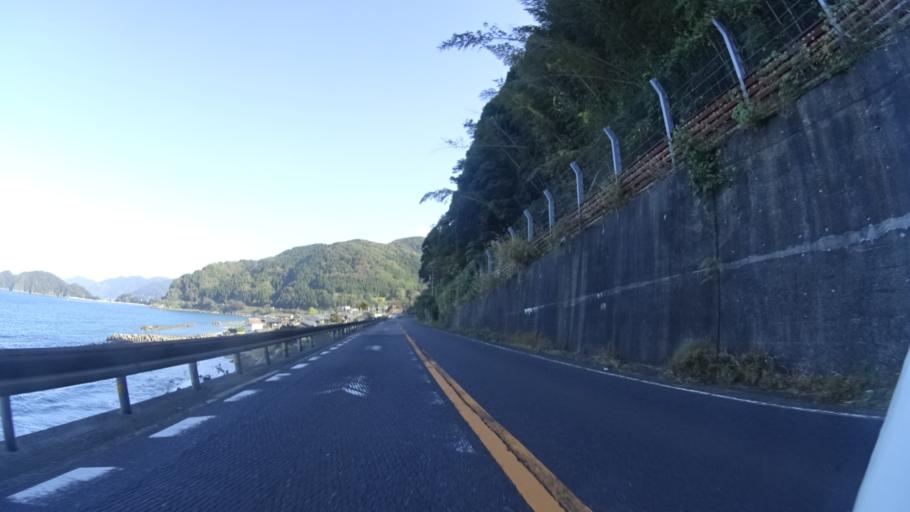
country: JP
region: Fukui
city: Tsuruga
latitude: 35.7194
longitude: 136.0947
